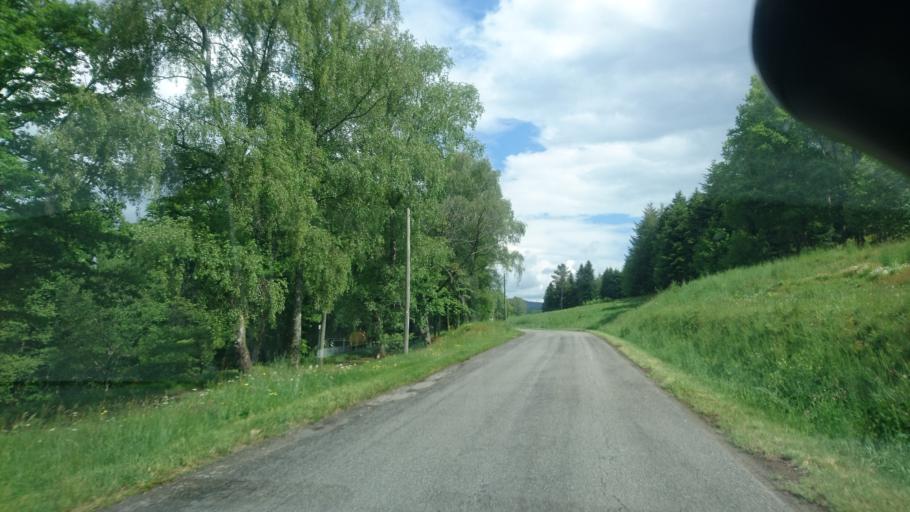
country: FR
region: Limousin
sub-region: Departement de la Haute-Vienne
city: Peyrat-le-Chateau
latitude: 45.7863
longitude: 1.8816
